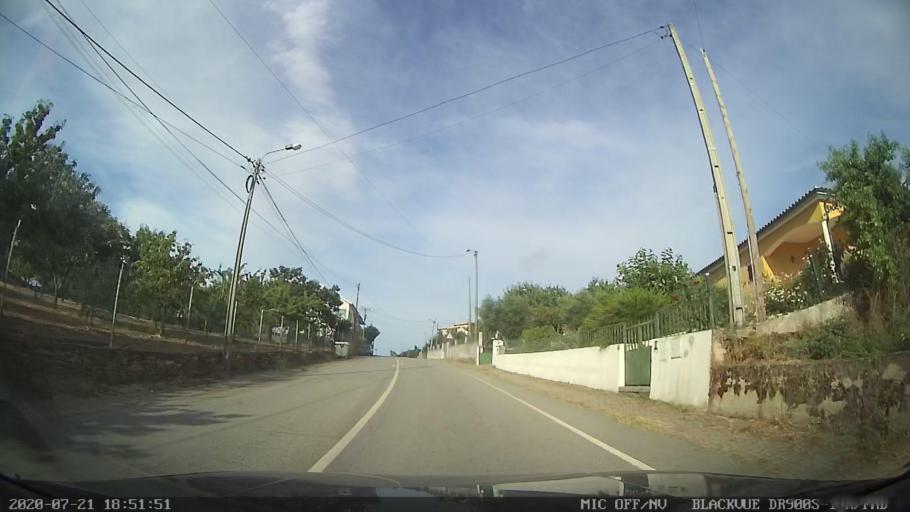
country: PT
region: Viseu
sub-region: Sao Joao da Pesqueira
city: Sao Joao da Pesqueira
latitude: 41.1451
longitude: -7.4181
